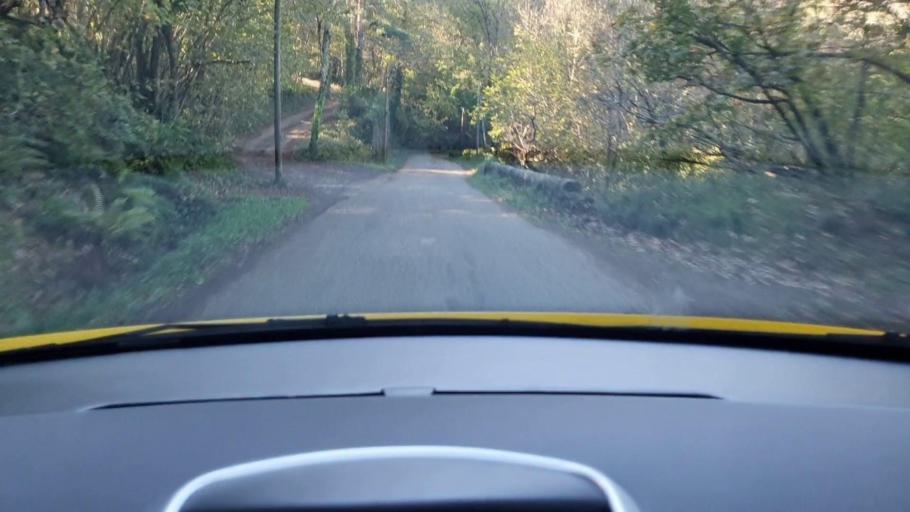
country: FR
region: Languedoc-Roussillon
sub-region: Departement du Gard
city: Sumene
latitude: 43.9812
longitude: 3.6800
